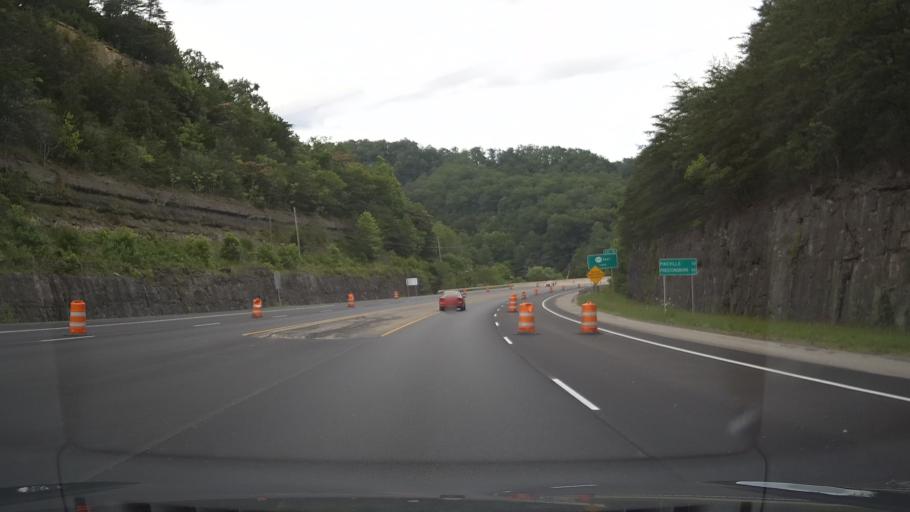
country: US
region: Kentucky
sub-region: Pike County
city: Pikeville
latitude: 37.3846
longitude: -82.5407
